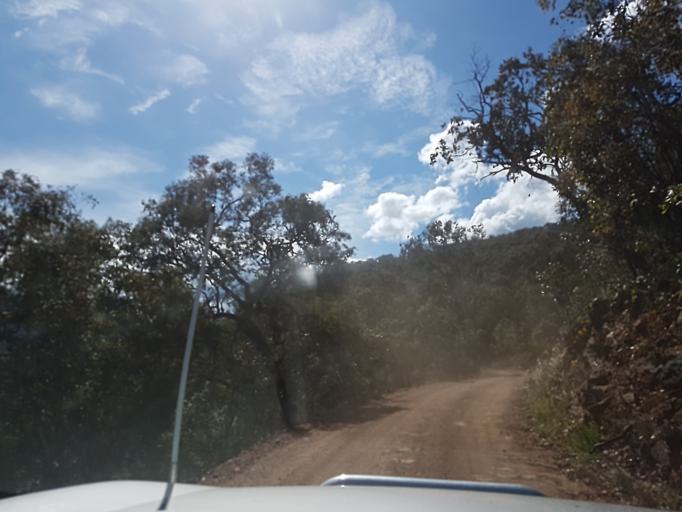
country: AU
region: Victoria
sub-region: Alpine
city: Mount Beauty
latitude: -37.3764
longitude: 147.0380
